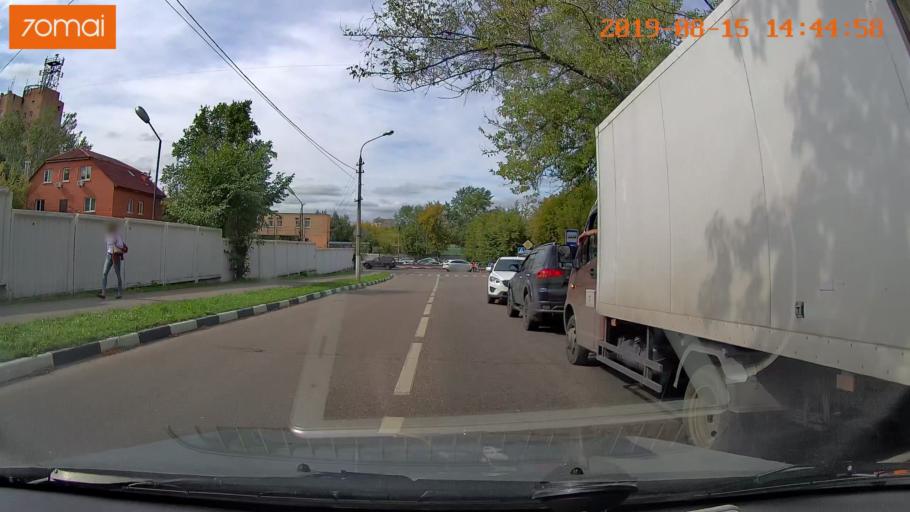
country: RU
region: Moskovskaya
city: Lyubertsy
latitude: 55.6717
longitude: 37.9017
